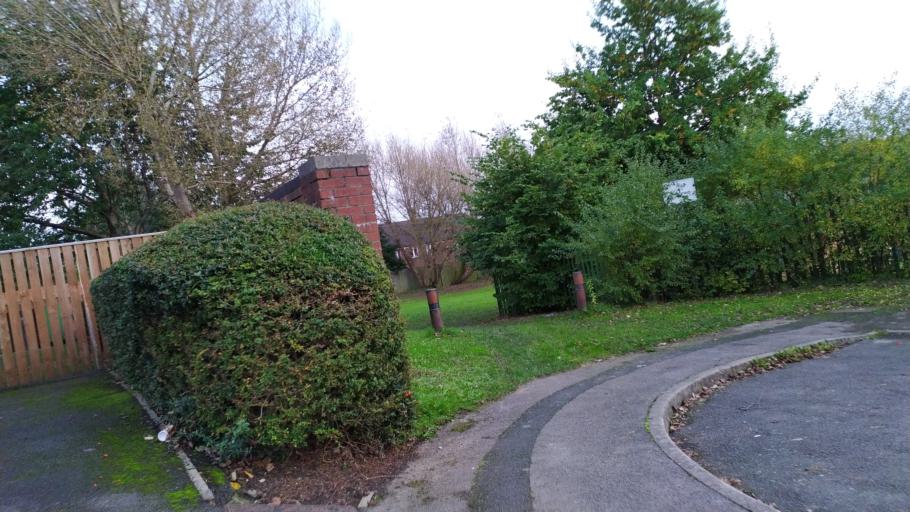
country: GB
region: England
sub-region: City and Borough of Leeds
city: Chapel Allerton
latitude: 53.8274
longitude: -1.5631
